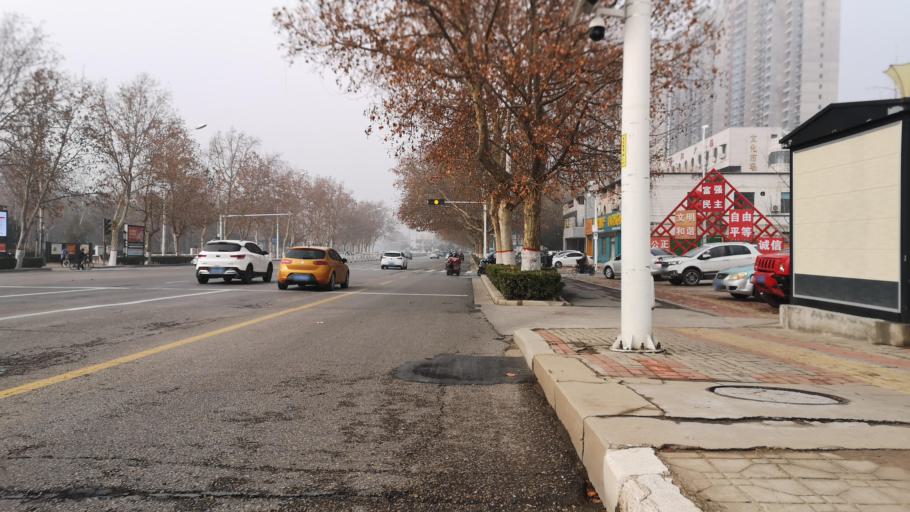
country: CN
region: Henan Sheng
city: Zhongyuanlu
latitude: 35.7801
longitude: 115.0487
